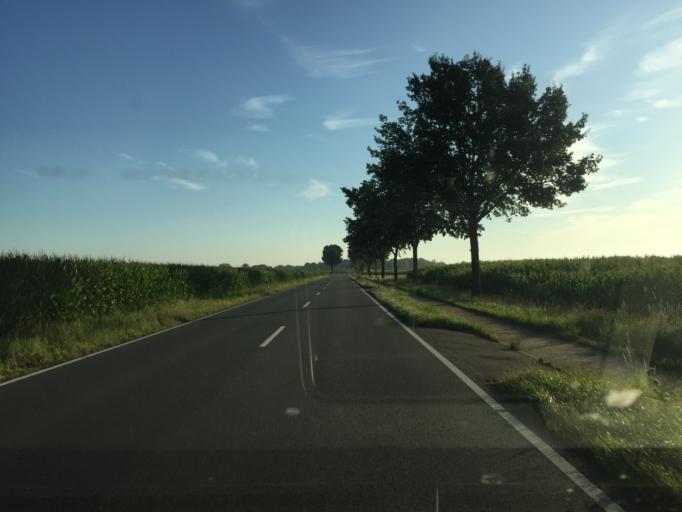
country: DE
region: Lower Saxony
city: Rethem
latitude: 52.7695
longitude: 9.3581
